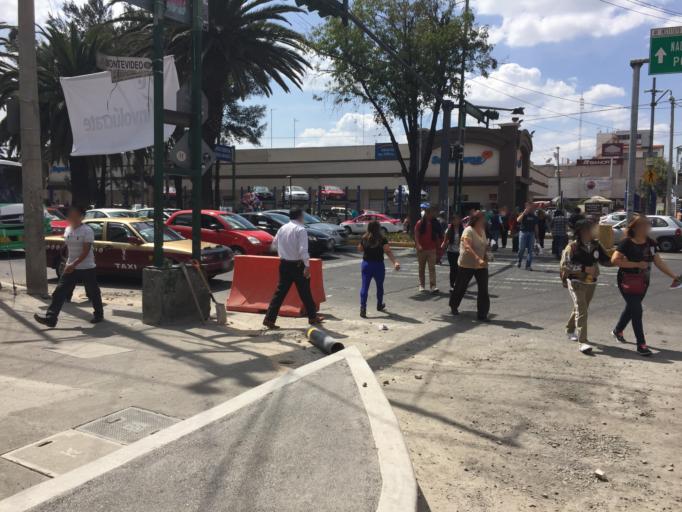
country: MX
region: Mexico
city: Colonia Lindavista
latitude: 19.4906
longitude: -99.1333
